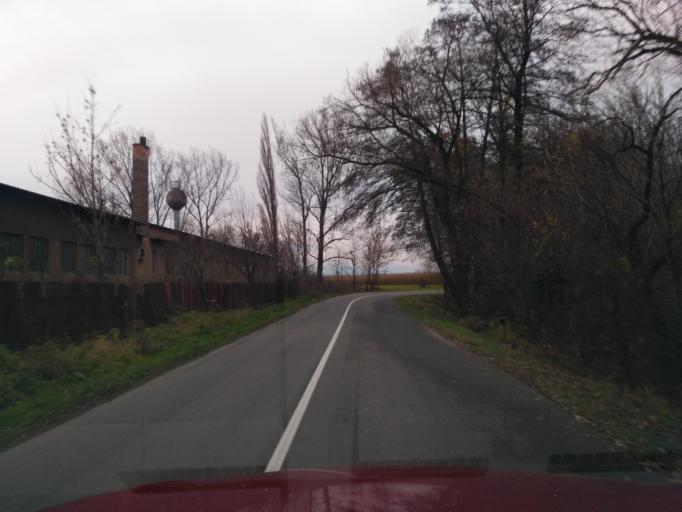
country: SK
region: Kosicky
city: Kosice
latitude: 48.5832
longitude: 21.1699
